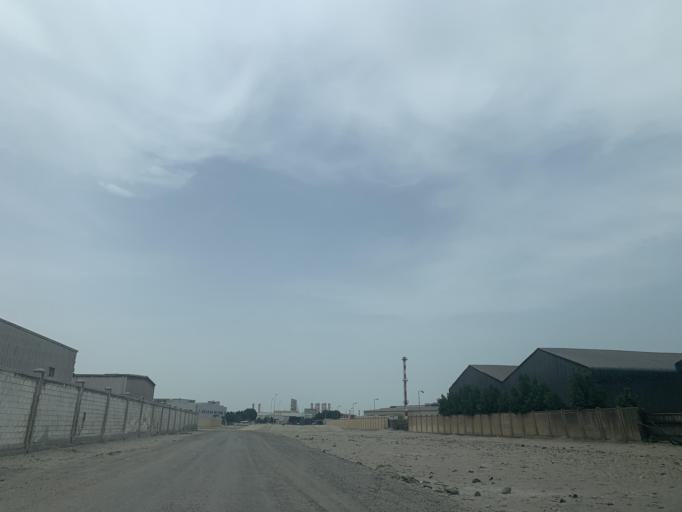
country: BH
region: Muharraq
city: Al Hadd
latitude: 26.2078
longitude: 50.6687
